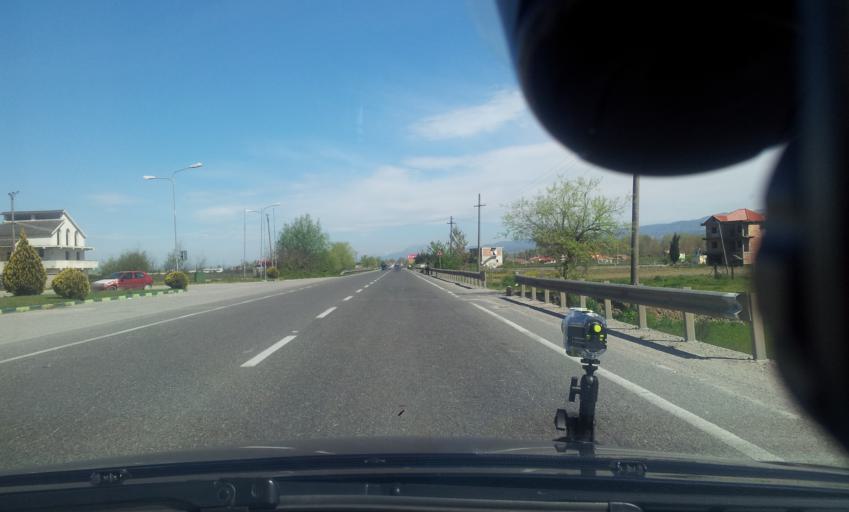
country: AL
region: Tirane
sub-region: Rrethi i Tiranes
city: Preze
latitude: 41.4438
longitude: 19.6886
